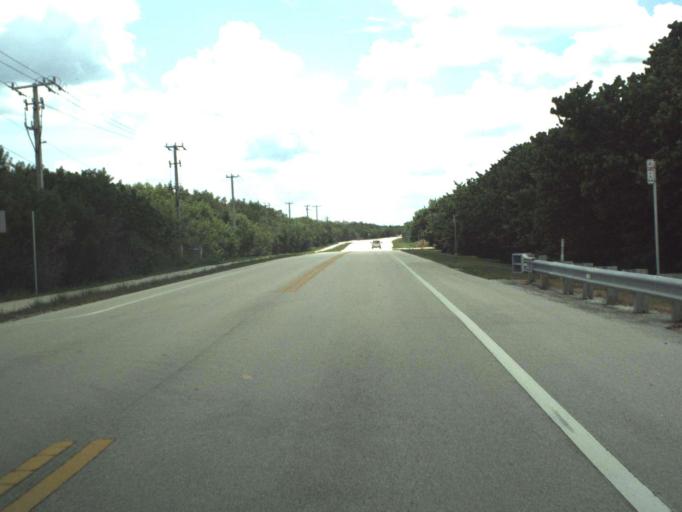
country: US
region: Florida
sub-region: Saint Lucie County
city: Hutchinson Island South
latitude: 27.3436
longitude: -80.2396
